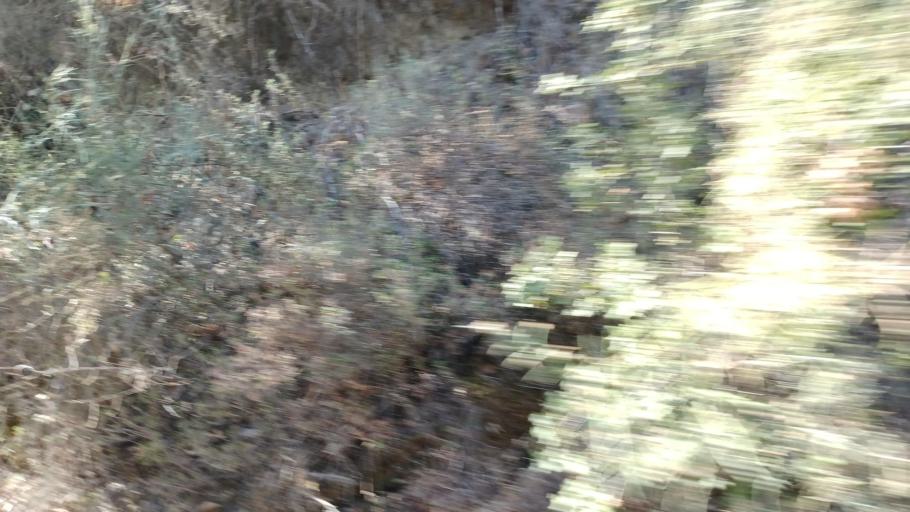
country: CY
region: Pafos
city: Pegeia
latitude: 34.9383
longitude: 32.4717
